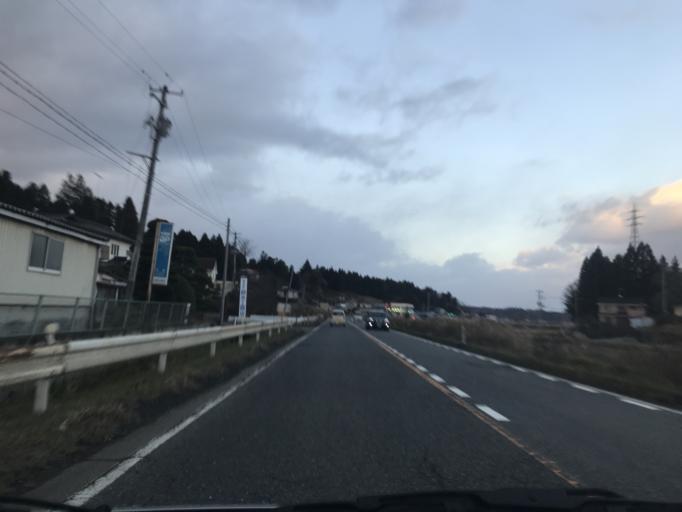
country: JP
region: Iwate
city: Ichinoseki
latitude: 38.7900
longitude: 141.0507
